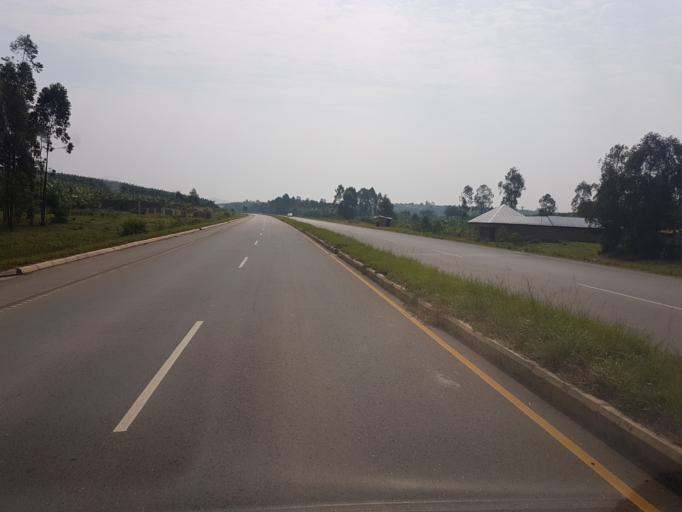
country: UG
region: Western Region
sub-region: Mbarara District
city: Bwizibwera
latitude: -0.6358
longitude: 30.5964
